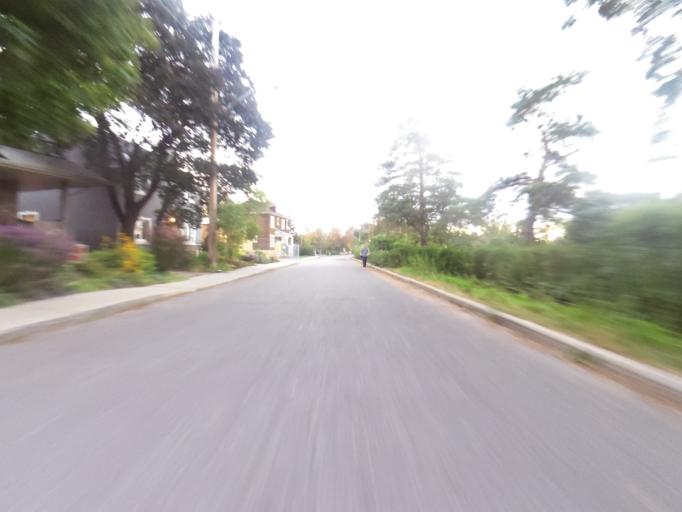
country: CA
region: Ontario
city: Ottawa
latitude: 45.3996
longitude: -75.6784
